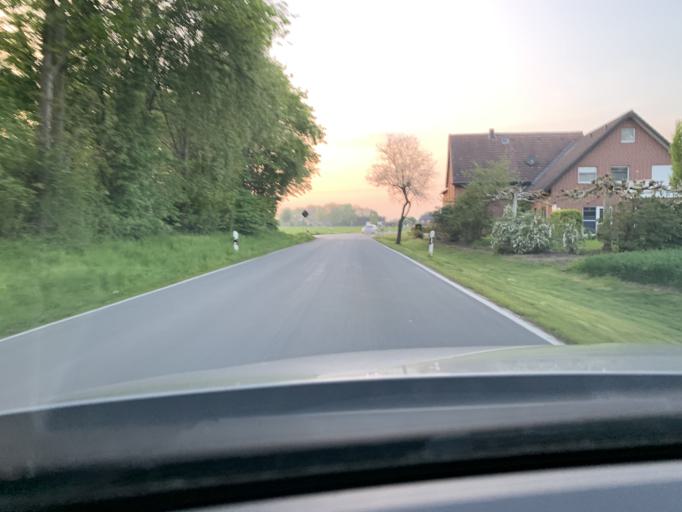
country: DE
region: North Rhine-Westphalia
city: Rietberg
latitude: 51.7753
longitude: 8.3790
